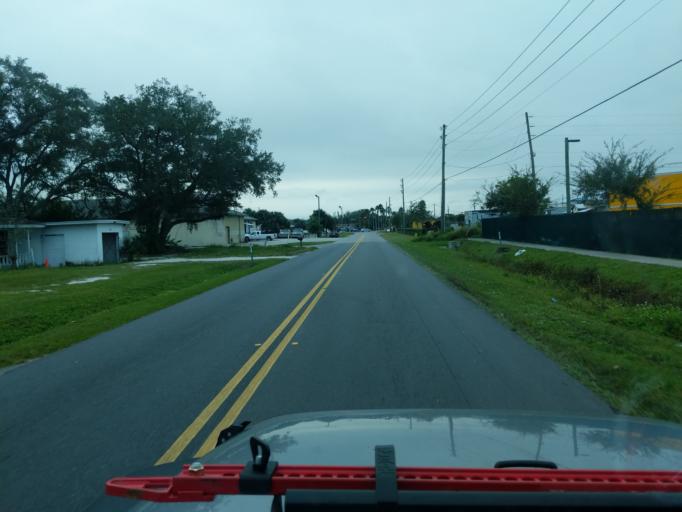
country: US
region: Florida
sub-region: Orange County
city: Winter Garden
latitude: 28.5536
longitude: -81.5648
